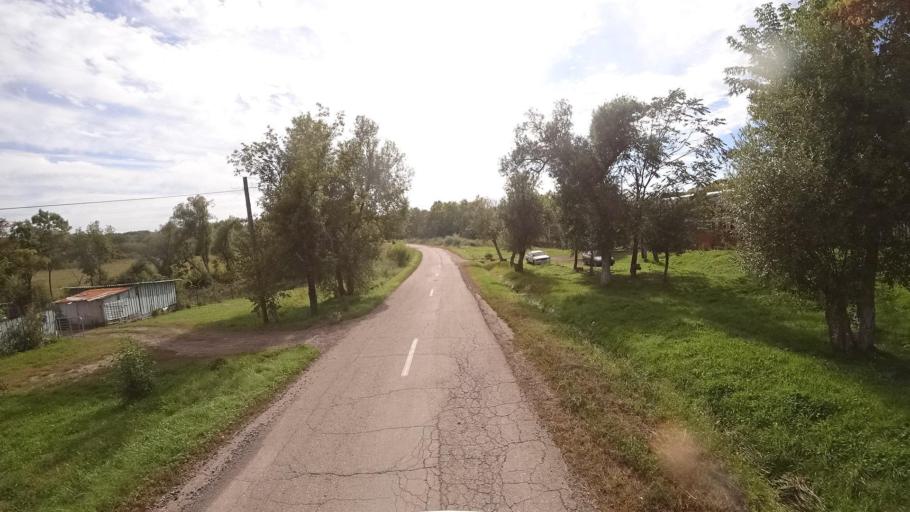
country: RU
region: Primorskiy
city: Dostoyevka
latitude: 44.3337
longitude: 133.4831
